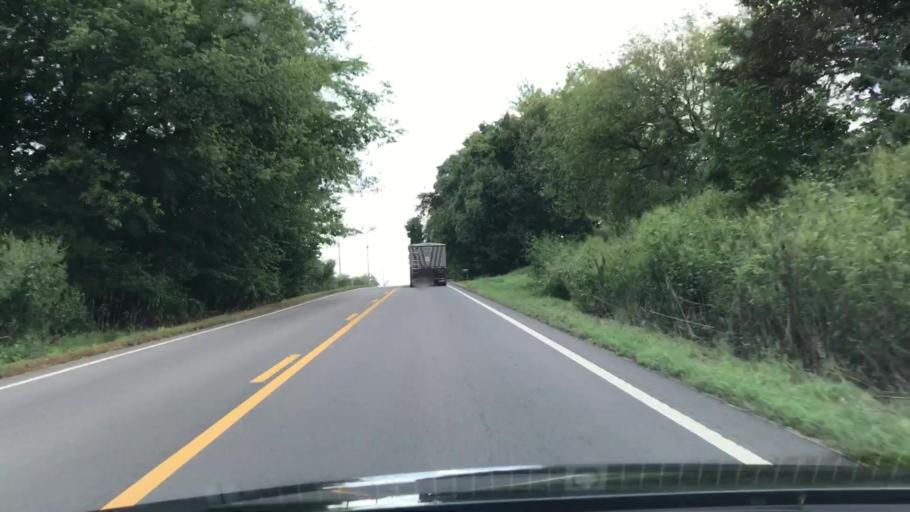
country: US
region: Tennessee
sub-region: Robertson County
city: Springfield
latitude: 36.6350
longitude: -86.9726
